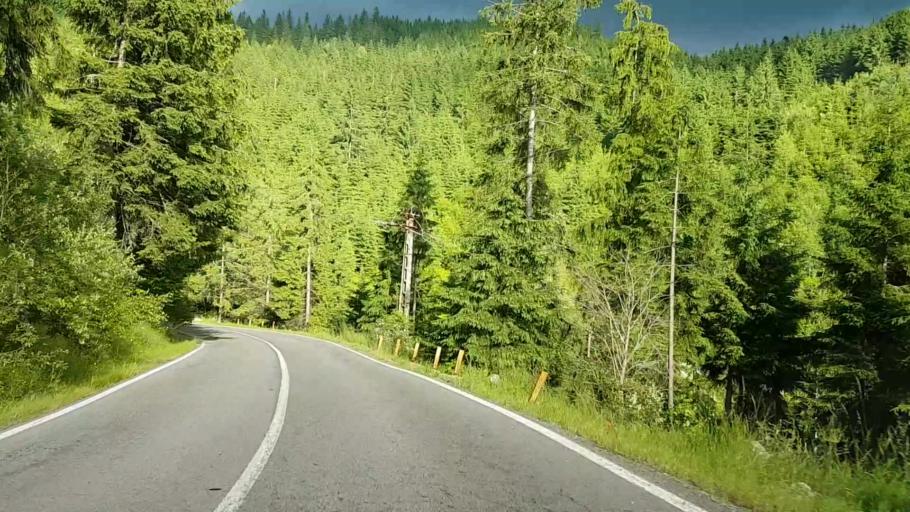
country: RO
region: Harghita
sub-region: Municipiul Gheorgheni
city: Gheorgheni
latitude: 46.7729
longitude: 25.7117
